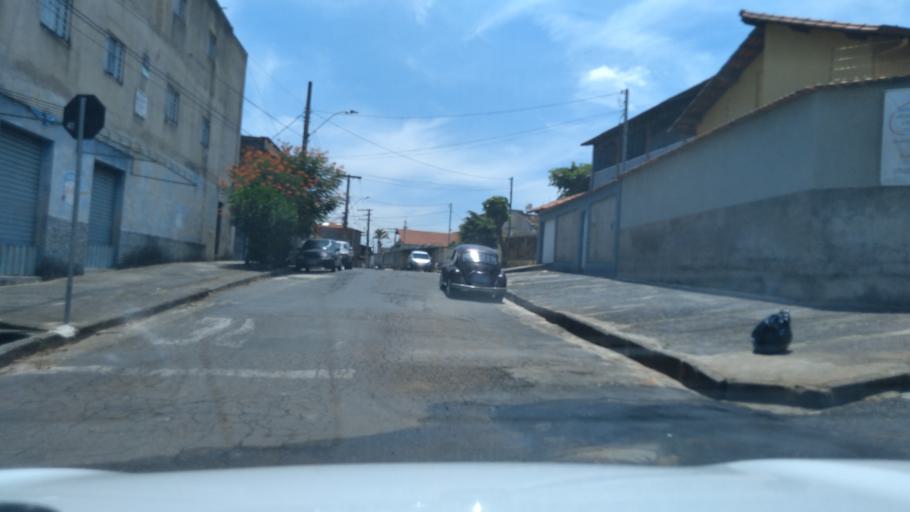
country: BR
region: Minas Gerais
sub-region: Contagem
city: Contagem
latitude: -19.9005
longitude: -44.0147
